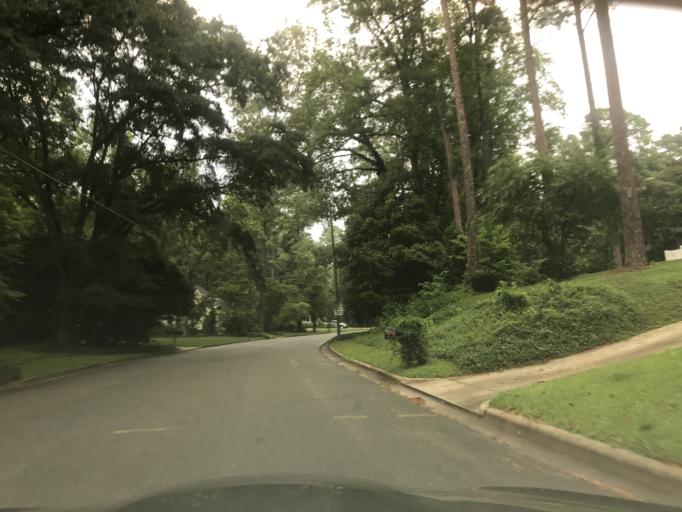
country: US
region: North Carolina
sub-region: Wake County
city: West Raleigh
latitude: 35.8377
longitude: -78.6562
